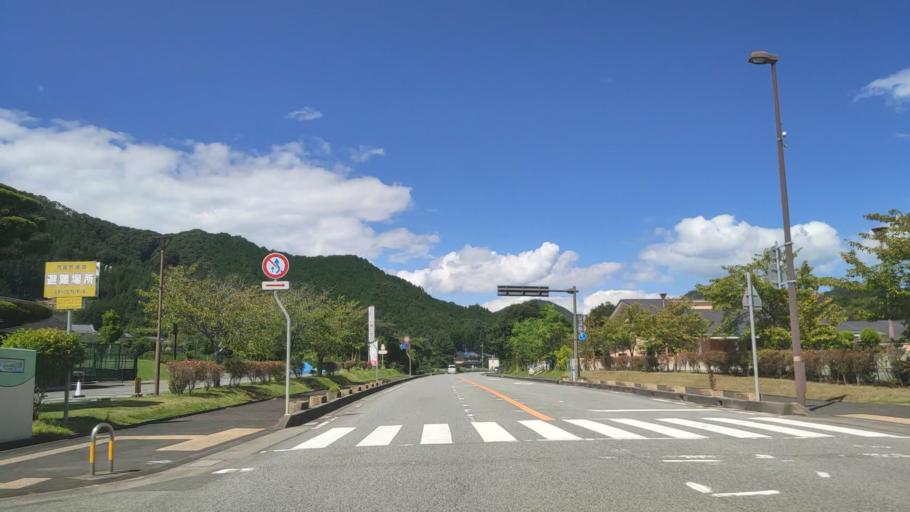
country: JP
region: Kyoto
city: Fukuchiyama
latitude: 35.2375
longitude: 135.1248
